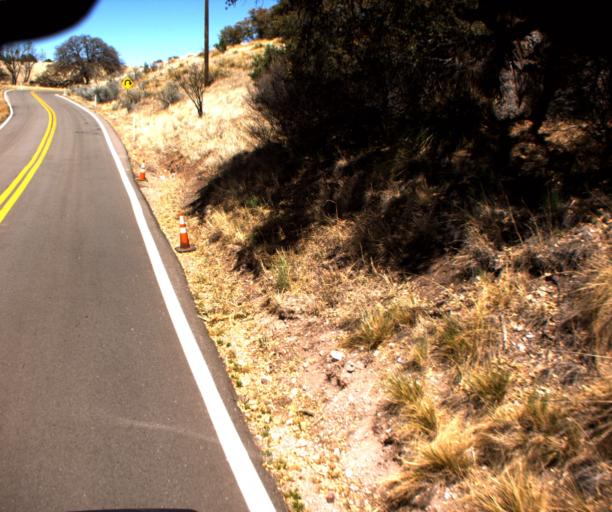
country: US
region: Arizona
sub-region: Cochise County
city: Huachuca City
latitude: 31.5431
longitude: -110.5255
